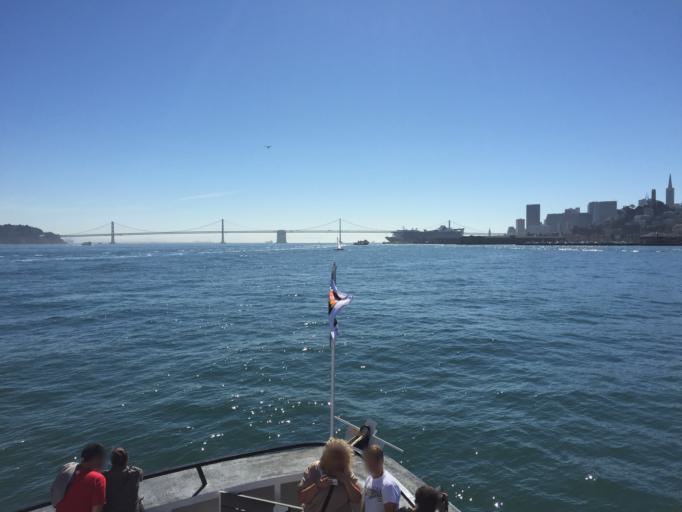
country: US
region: California
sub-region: San Francisco County
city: San Francisco
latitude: 37.8174
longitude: -122.4136
